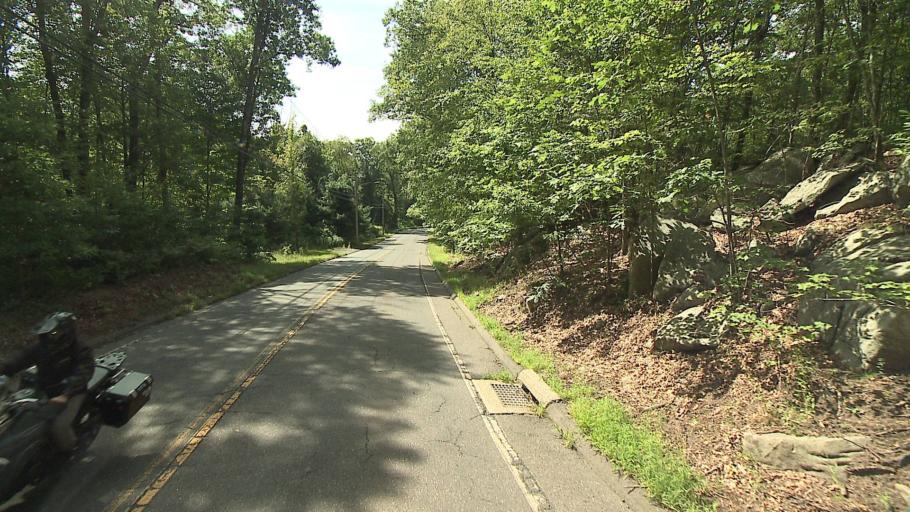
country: US
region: Connecticut
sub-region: Litchfield County
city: Oakville
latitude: 41.6233
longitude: -73.0489
